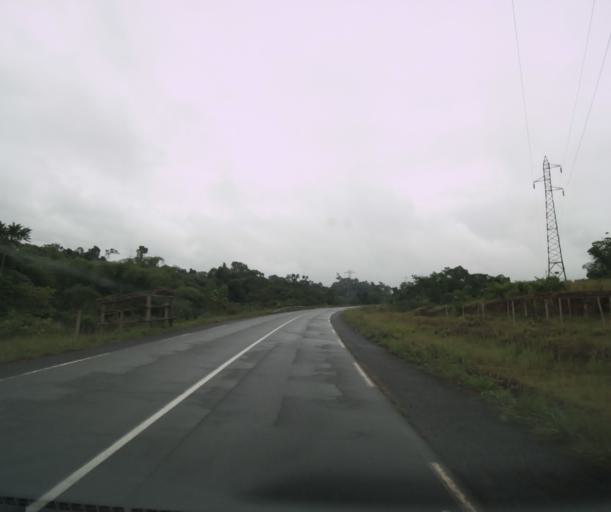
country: CM
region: Littoral
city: Dizangue
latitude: 3.3716
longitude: 10.1033
